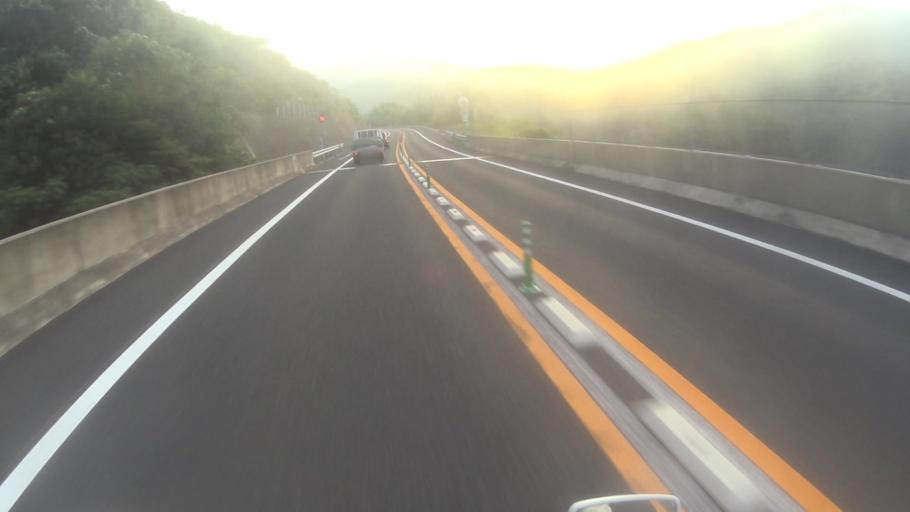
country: JP
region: Kyoto
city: Miyazu
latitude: 35.5013
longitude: 135.1794
